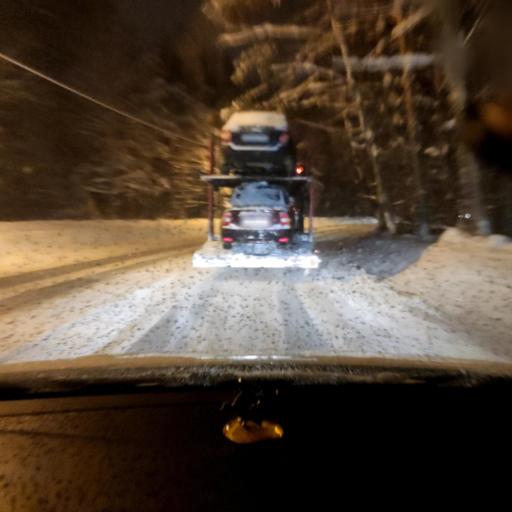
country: RU
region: Tatarstan
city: Osinovo
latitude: 55.8297
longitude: 48.8926
